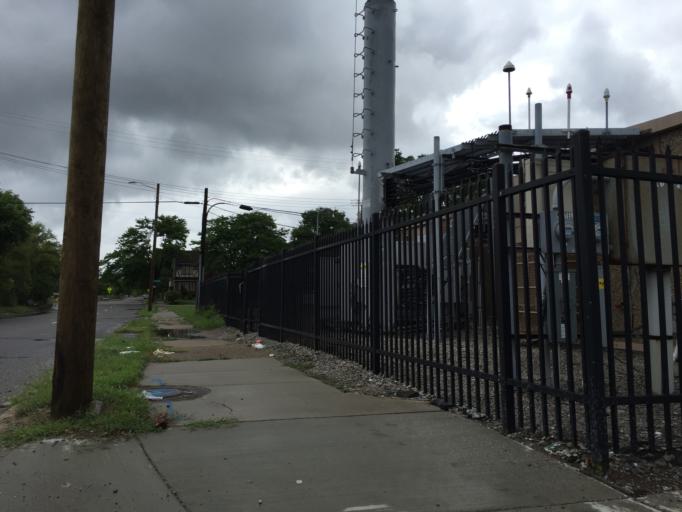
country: US
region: Michigan
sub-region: Oakland County
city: Oak Park
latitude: 42.4043
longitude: -83.1597
